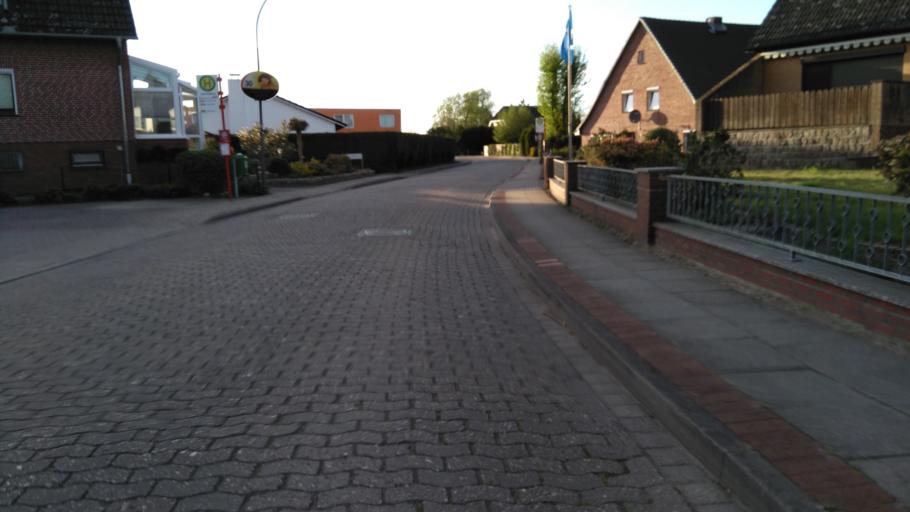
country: DE
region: Lower Saxony
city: Buxtehude
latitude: 53.4744
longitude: 9.6628
